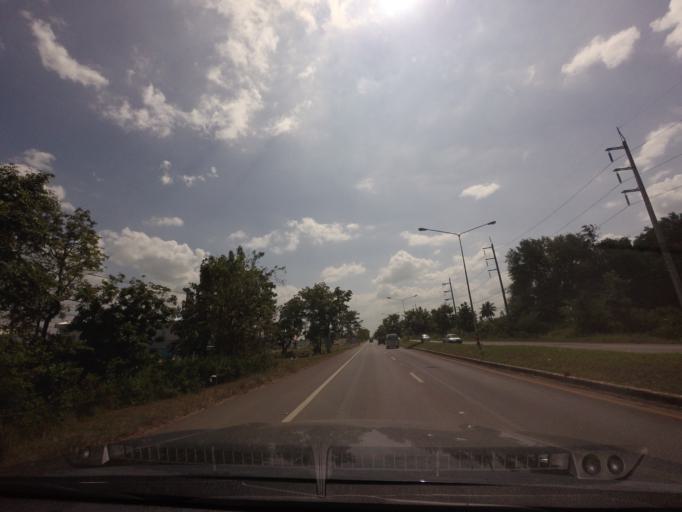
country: TH
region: Phetchabun
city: Nong Phai
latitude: 15.8986
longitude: 101.0274
